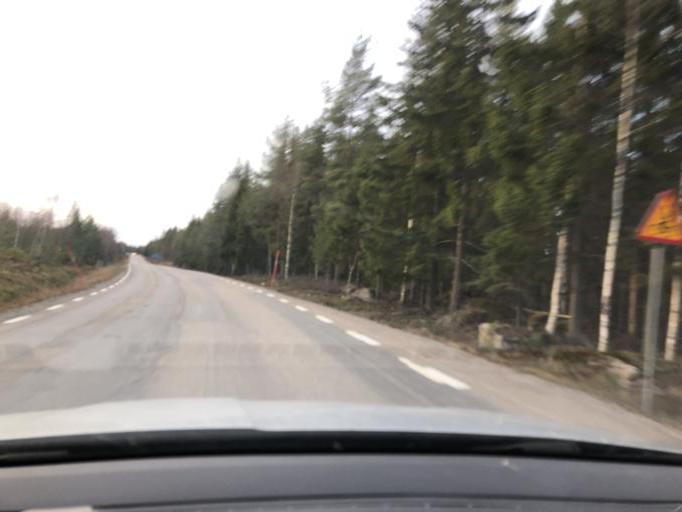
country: SE
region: Gaevleborg
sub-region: Hudiksvalls Kommun
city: Iggesund
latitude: 61.5516
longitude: 16.9891
